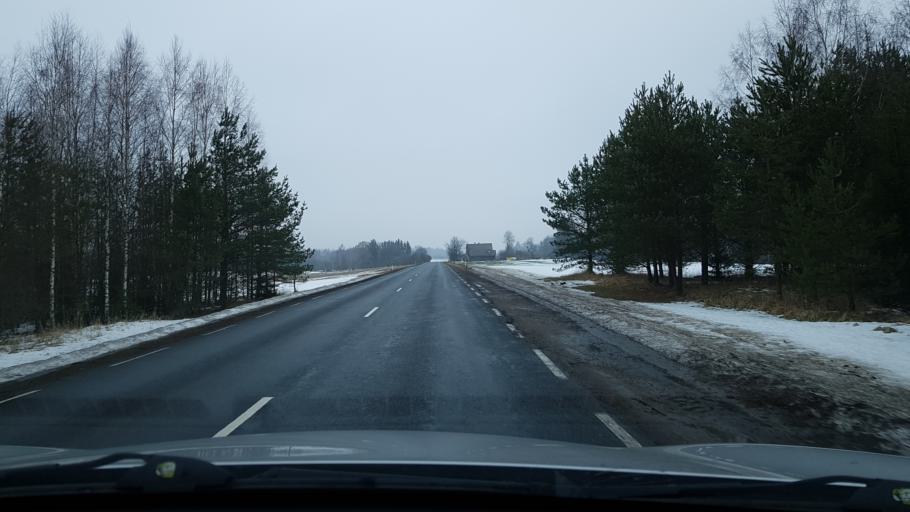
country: EE
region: Valgamaa
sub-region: Torva linn
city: Torva
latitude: 58.1239
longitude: 25.9925
